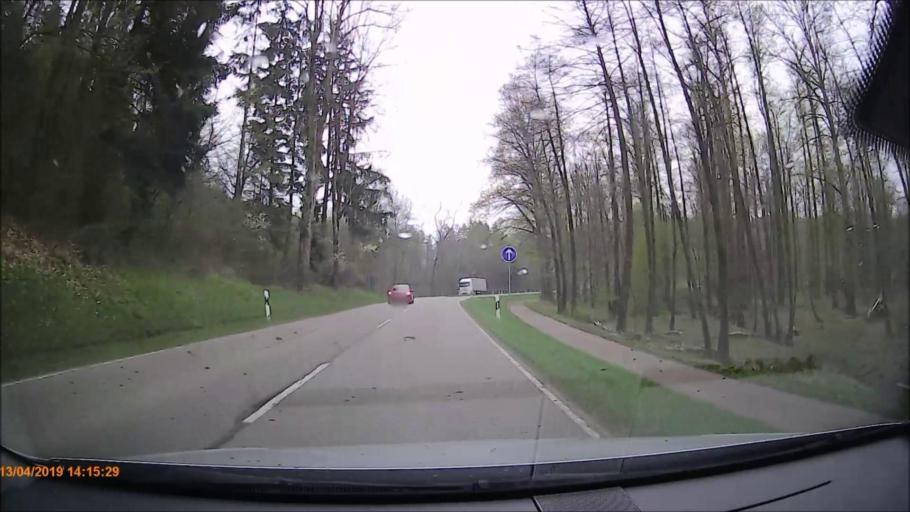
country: DE
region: Baden-Wuerttemberg
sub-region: Regierungsbezirk Stuttgart
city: Oberrot
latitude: 48.9979
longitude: 9.6868
